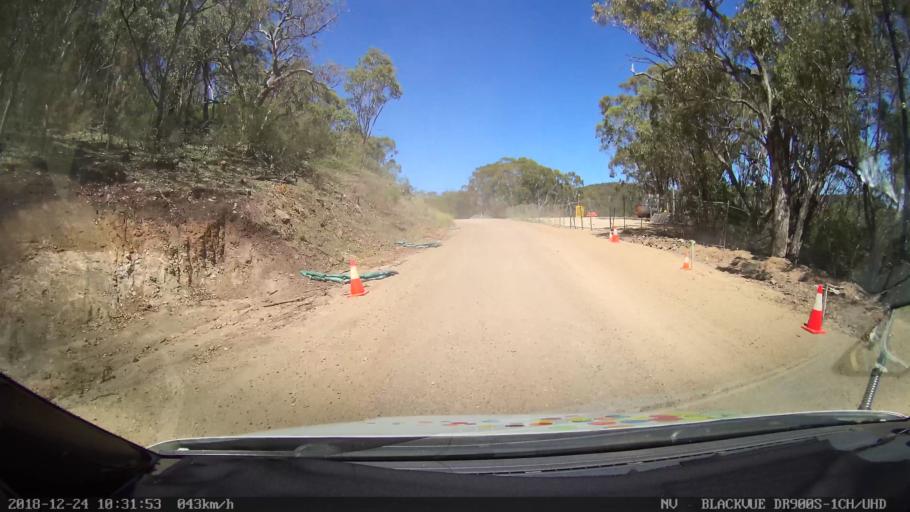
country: AU
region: New South Wales
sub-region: Upper Hunter Shire
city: Merriwa
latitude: -31.8397
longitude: 150.5192
